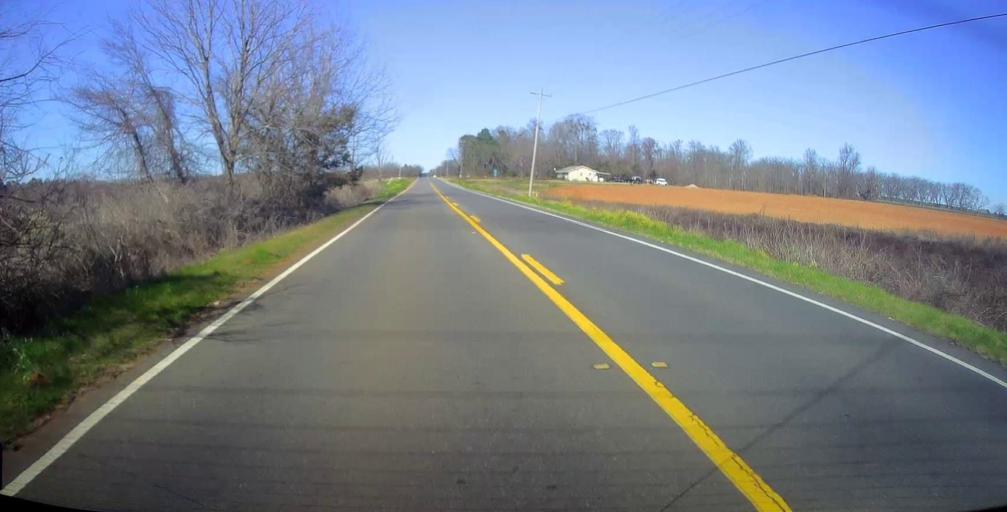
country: US
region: Georgia
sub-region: Macon County
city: Montezuma
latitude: 32.3283
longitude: -84.0219
